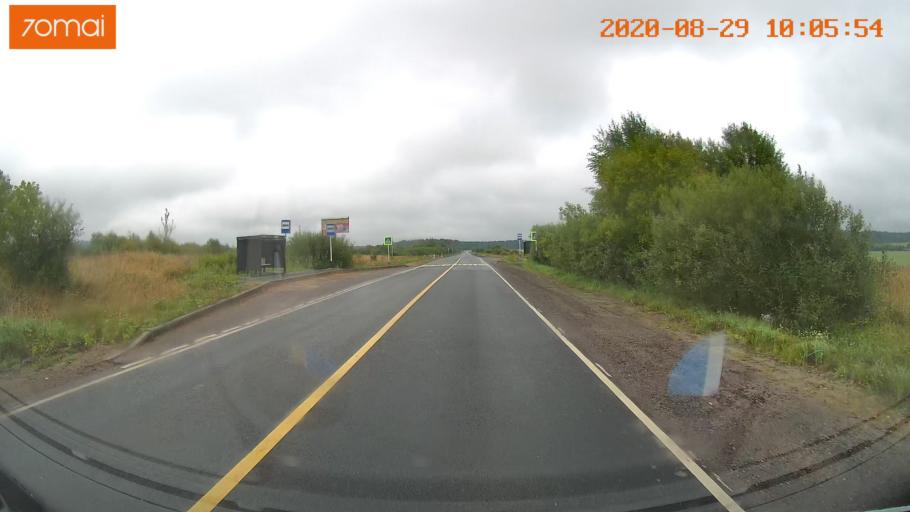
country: RU
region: Ivanovo
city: Zarechnyy
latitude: 57.3911
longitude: 42.5329
